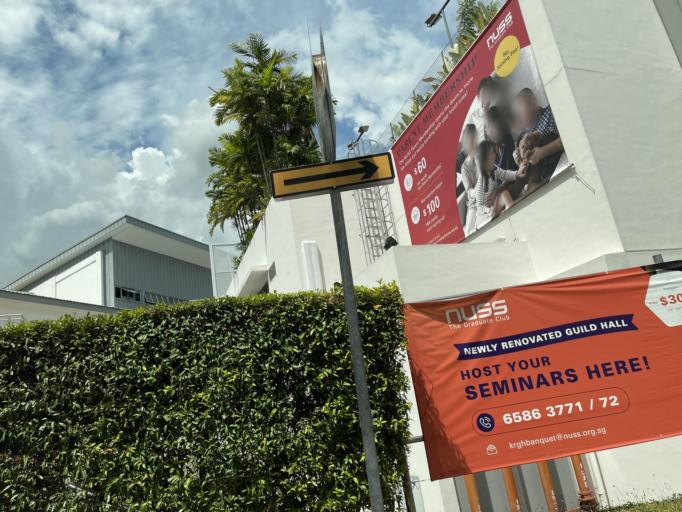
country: SG
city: Singapore
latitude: 1.2933
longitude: 103.7727
